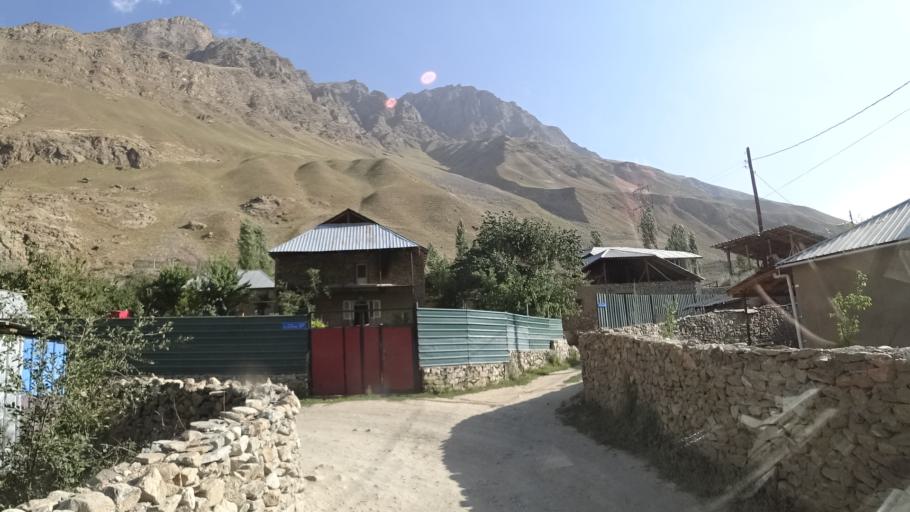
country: TJ
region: Gorno-Badakhshan
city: Khorugh
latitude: 37.4875
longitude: 71.5576
